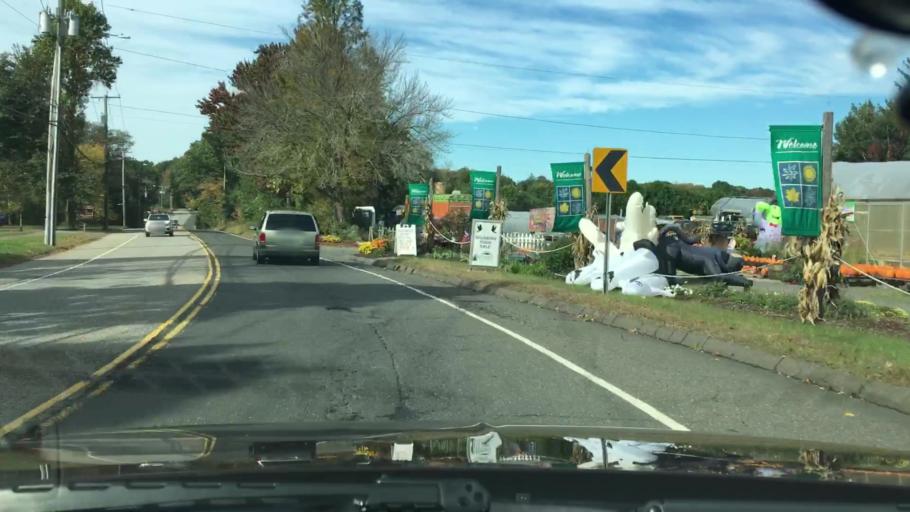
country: US
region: Connecticut
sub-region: Hartford County
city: Bristol
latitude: 41.6817
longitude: -72.9724
